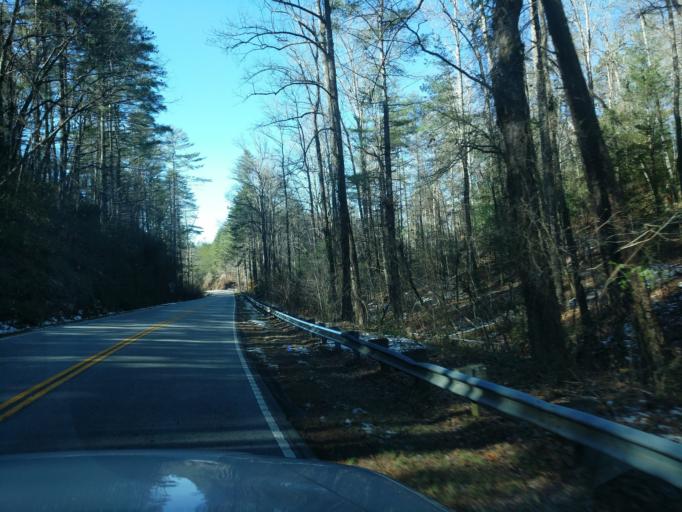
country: US
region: Georgia
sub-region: Rabun County
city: Clayton
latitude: 34.8102
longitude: -83.2921
